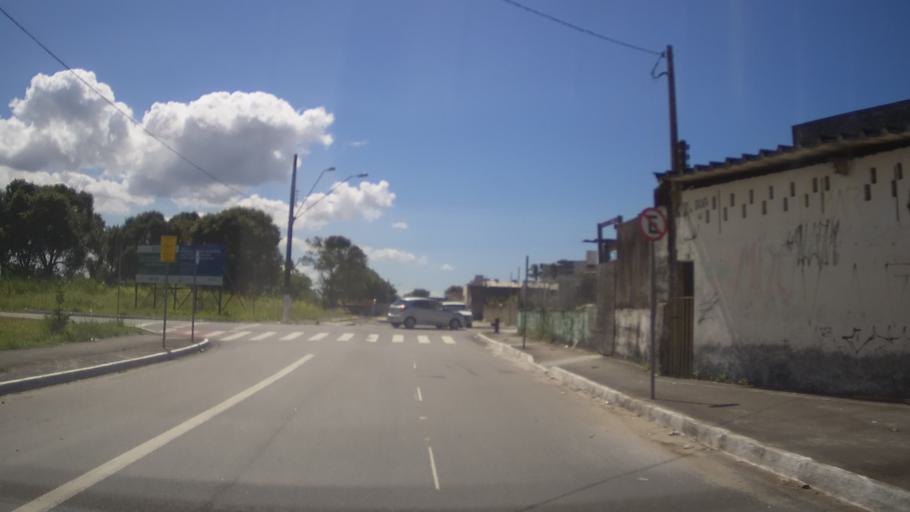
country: BR
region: Sao Paulo
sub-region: Mongagua
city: Mongagua
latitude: -24.0491
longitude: -46.5378
